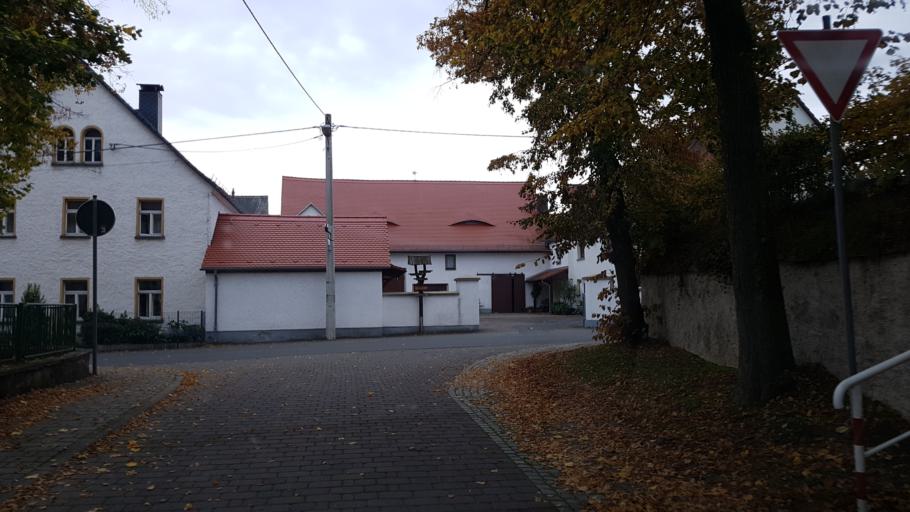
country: DE
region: Saxony
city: Dahlen
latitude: 51.3978
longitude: 12.9854
